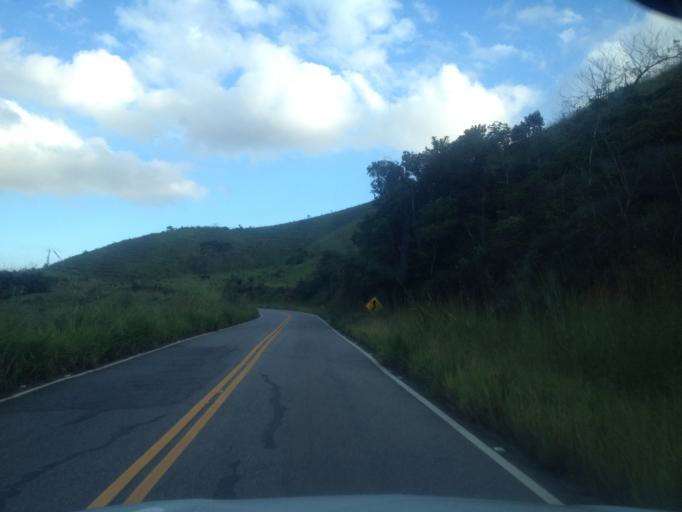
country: BR
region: Rio de Janeiro
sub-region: Quatis
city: Quatis
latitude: -22.3763
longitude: -44.2622
